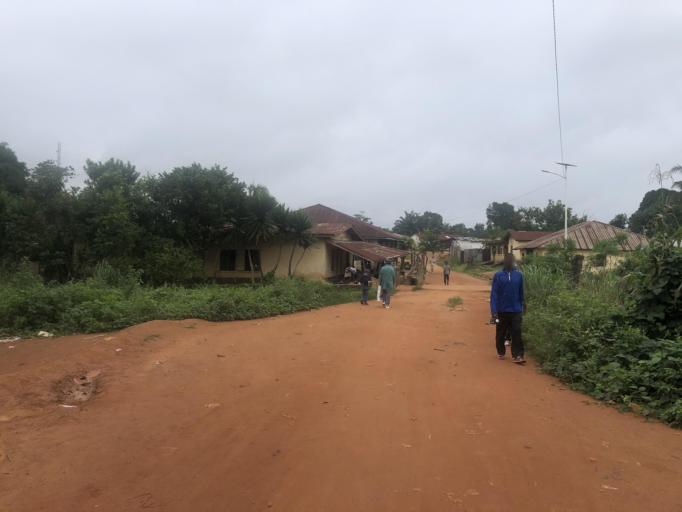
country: SL
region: Eastern Province
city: Kailahun
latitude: 8.2789
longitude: -10.5709
